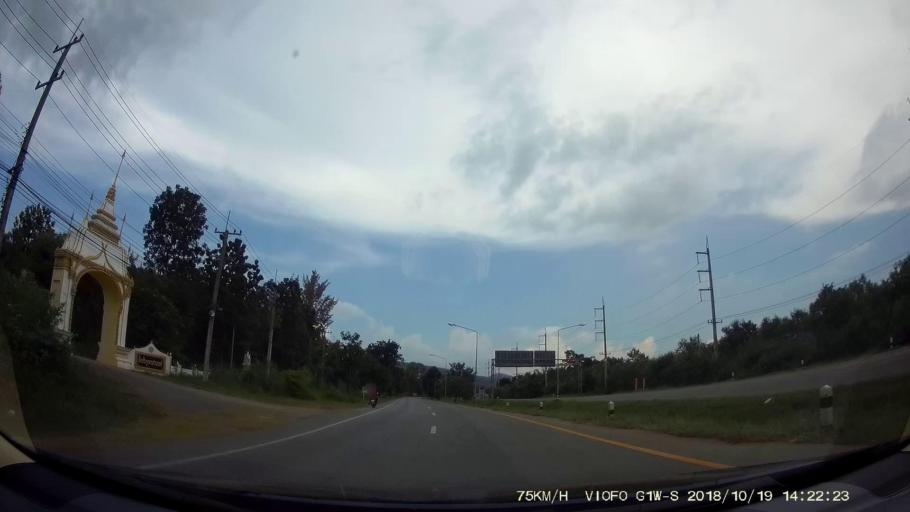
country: TH
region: Chaiyaphum
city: Kaeng Khro
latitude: 16.0621
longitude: 102.2748
